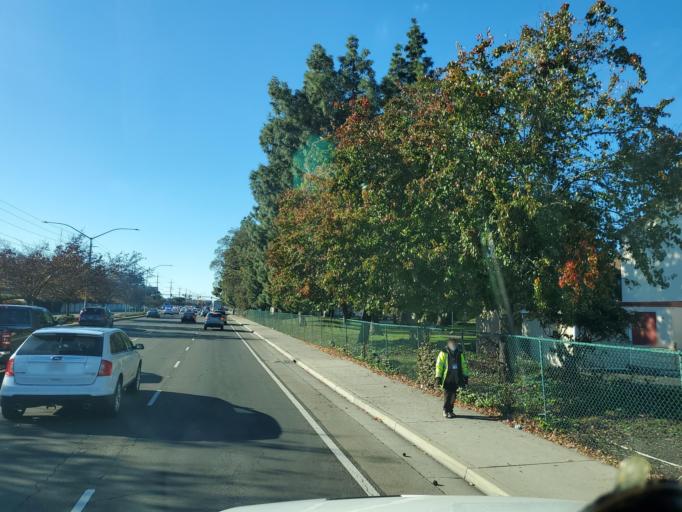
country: US
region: California
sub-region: San Joaquin County
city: Lincoln Village
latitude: 38.0210
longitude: -121.3120
